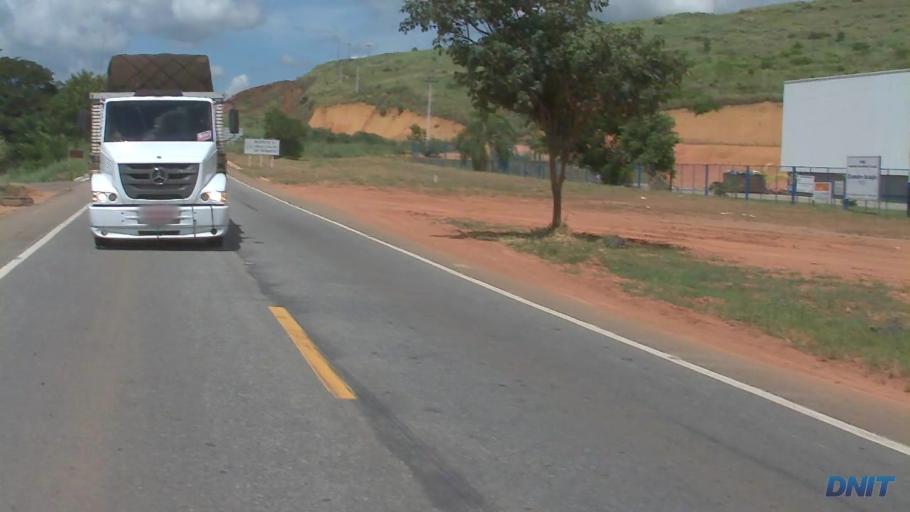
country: BR
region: Minas Gerais
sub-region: Governador Valadares
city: Governador Valadares
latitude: -18.9259
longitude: -42.0371
